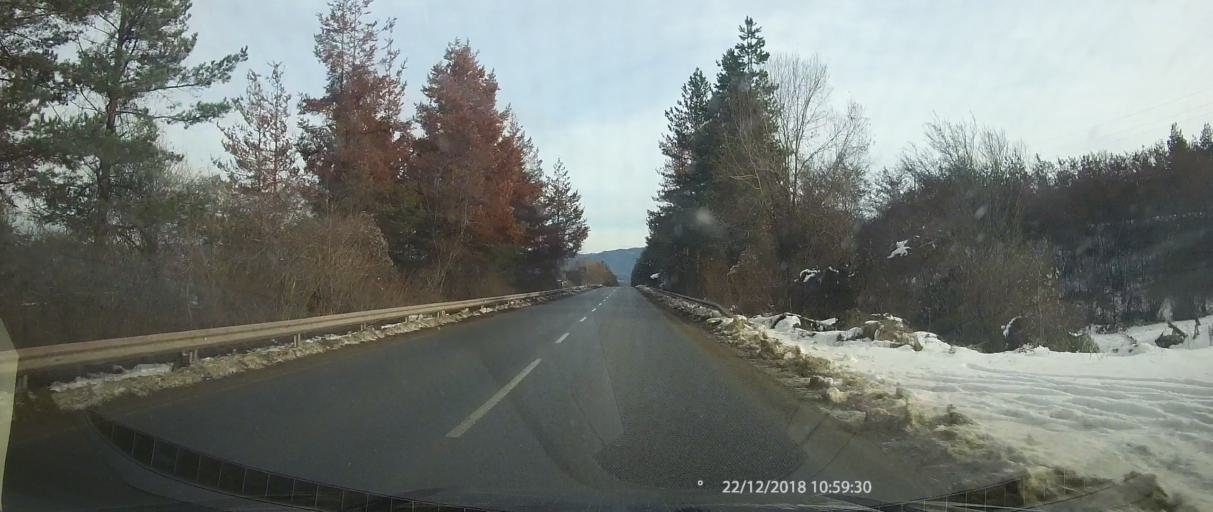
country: MK
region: Kriva Palanka
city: Kriva Palanka
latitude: 42.2257
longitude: 22.4815
